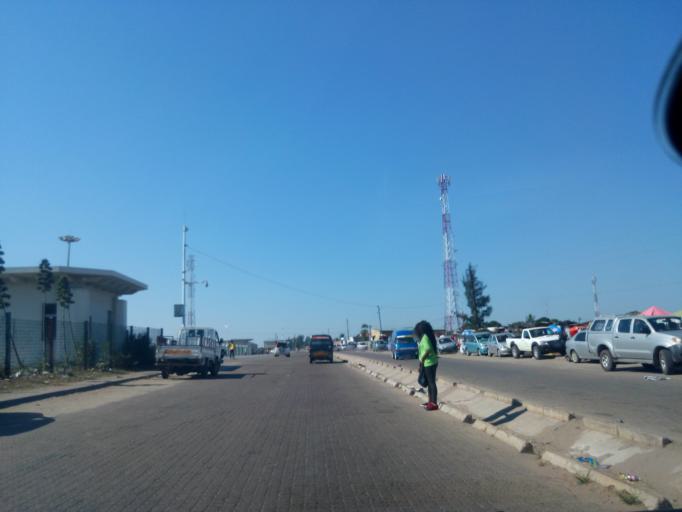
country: MZ
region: Maputo City
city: Maputo
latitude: -25.8300
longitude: 32.5741
